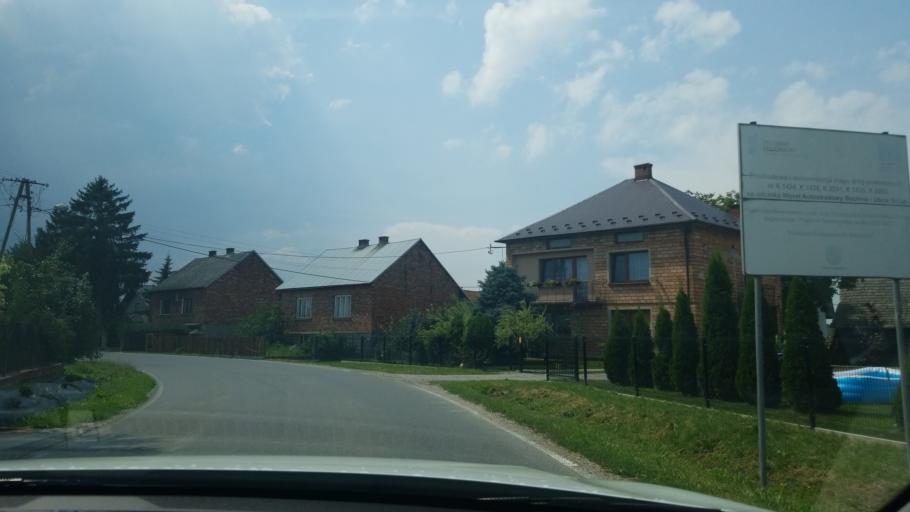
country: PL
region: Lesser Poland Voivodeship
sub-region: Powiat bochenski
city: Dziewin
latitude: 50.1029
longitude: 20.5114
